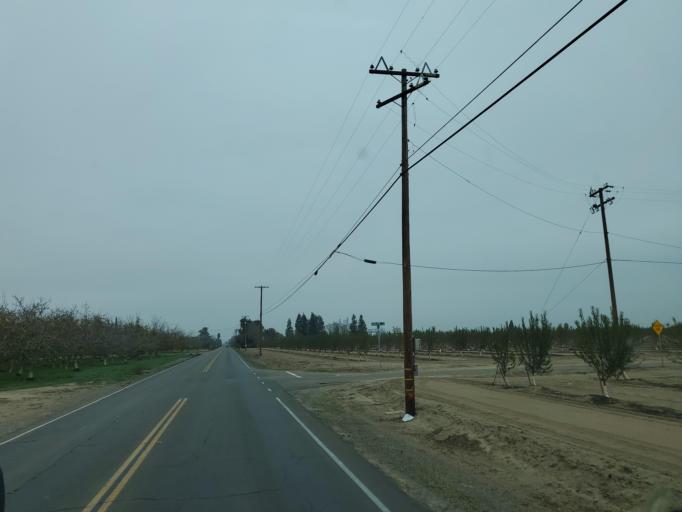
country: US
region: California
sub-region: Stanislaus County
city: Hughson
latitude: 37.5581
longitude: -120.8470
